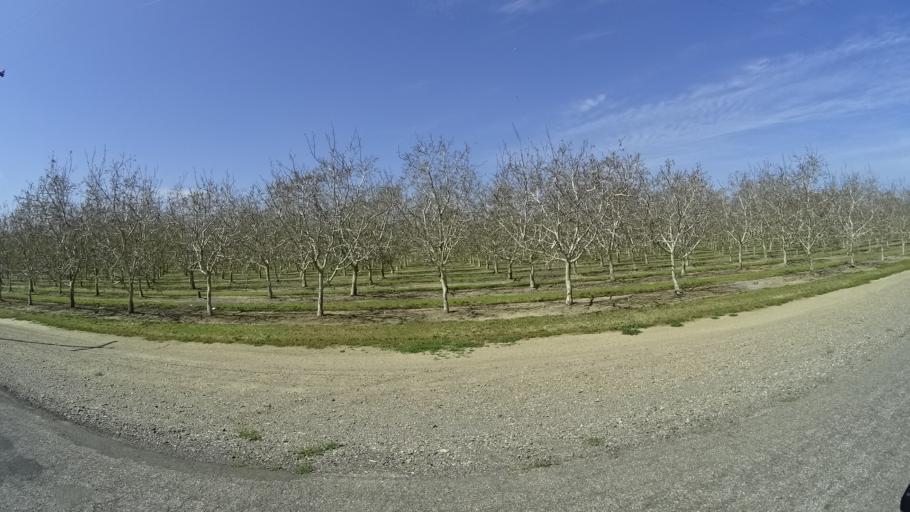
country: US
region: California
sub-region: Glenn County
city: Hamilton City
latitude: 39.6427
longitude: -122.0743
